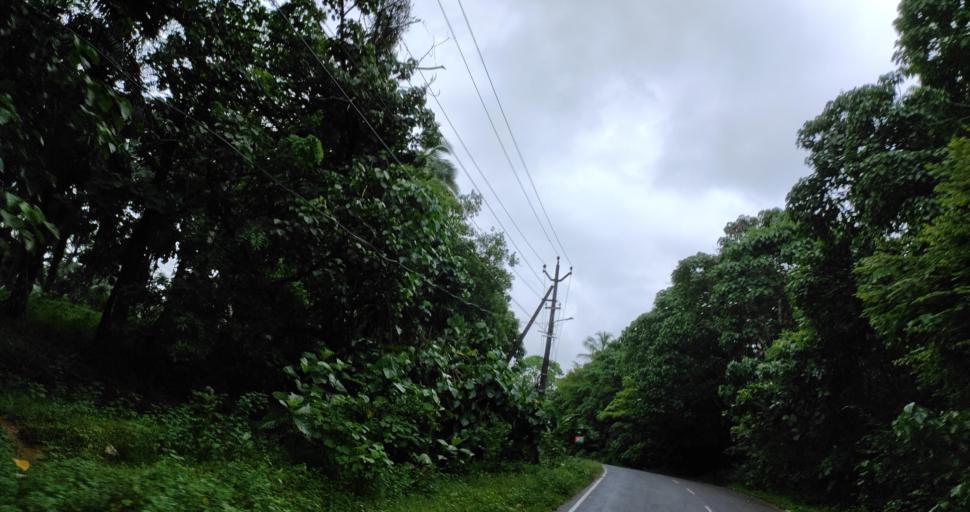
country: IN
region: Kerala
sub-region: Ernakulam
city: Angamali
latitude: 10.2878
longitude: 76.5532
